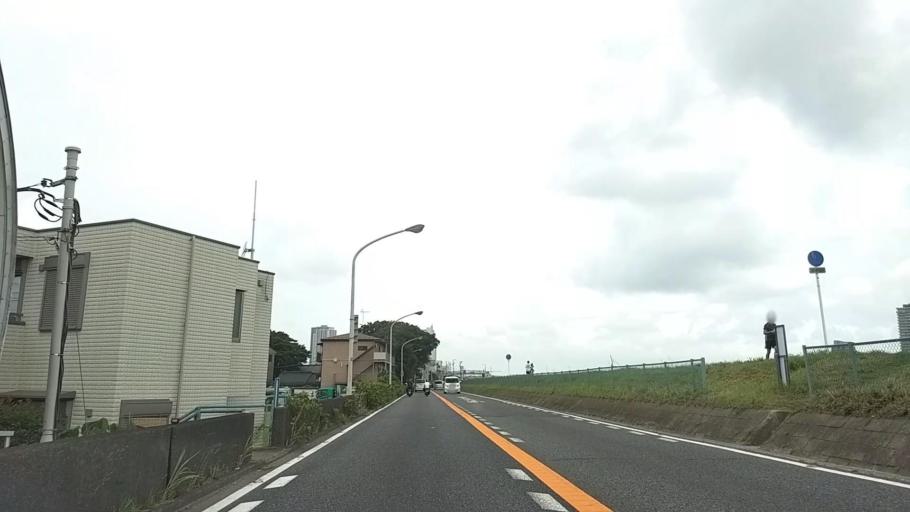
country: JP
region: Kanagawa
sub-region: Kawasaki-shi
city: Kawasaki
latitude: 35.5597
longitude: 139.6804
